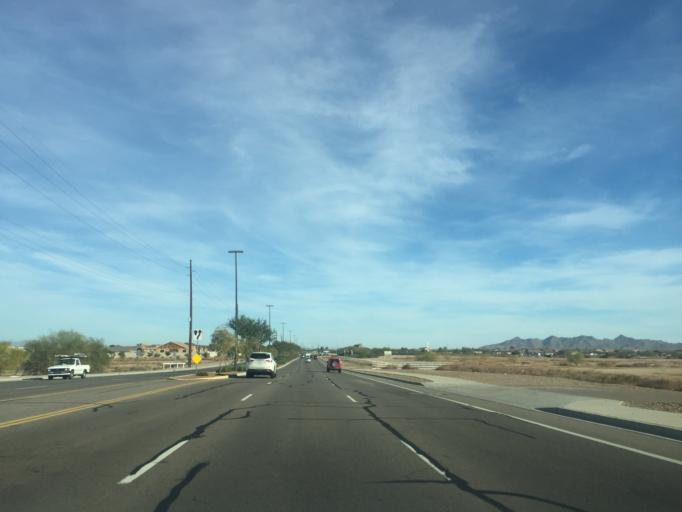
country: US
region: Arizona
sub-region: Maricopa County
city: Queen Creek
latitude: 33.2193
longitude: -111.7397
